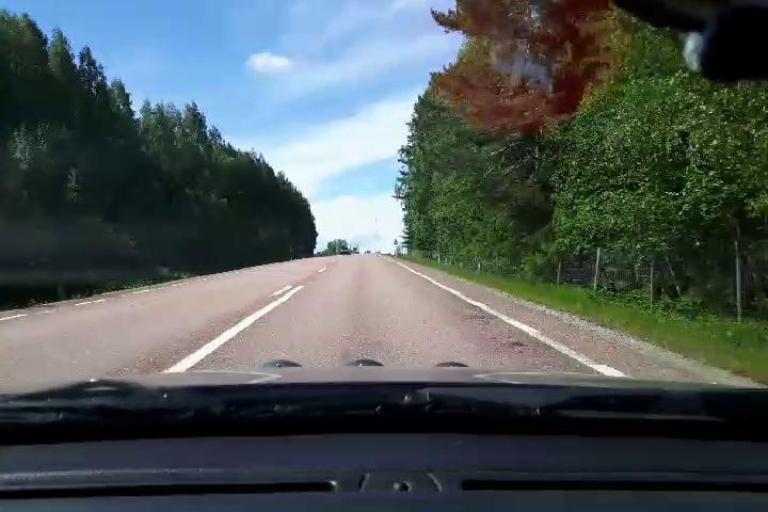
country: SE
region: Gaevleborg
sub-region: Bollnas Kommun
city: Kilafors
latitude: 61.1995
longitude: 16.7605
